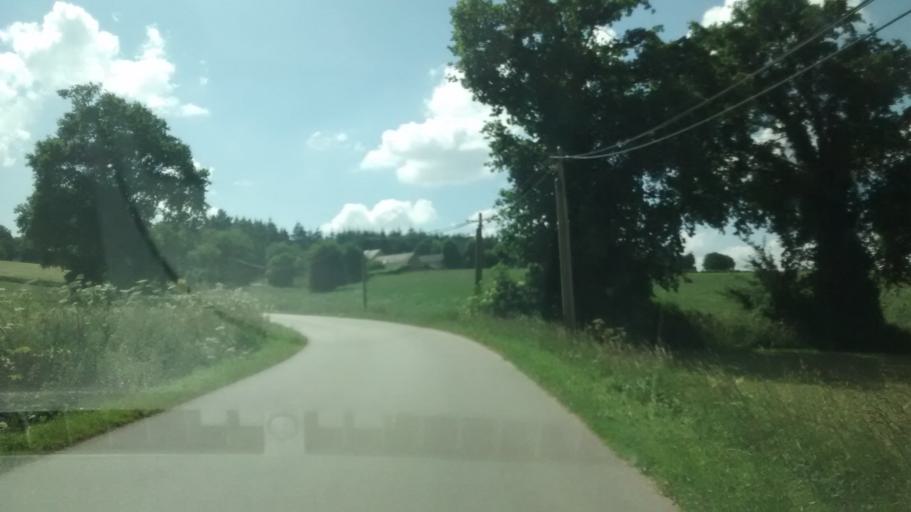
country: FR
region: Brittany
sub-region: Departement du Morbihan
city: Caro
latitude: 47.8666
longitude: -2.3145
